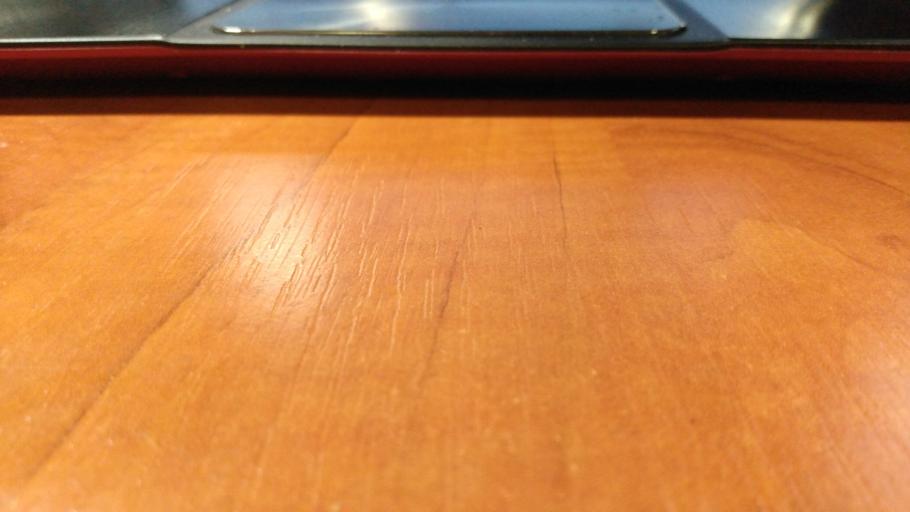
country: RU
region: Vologda
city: Babayevo
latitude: 59.1955
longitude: 36.1303
